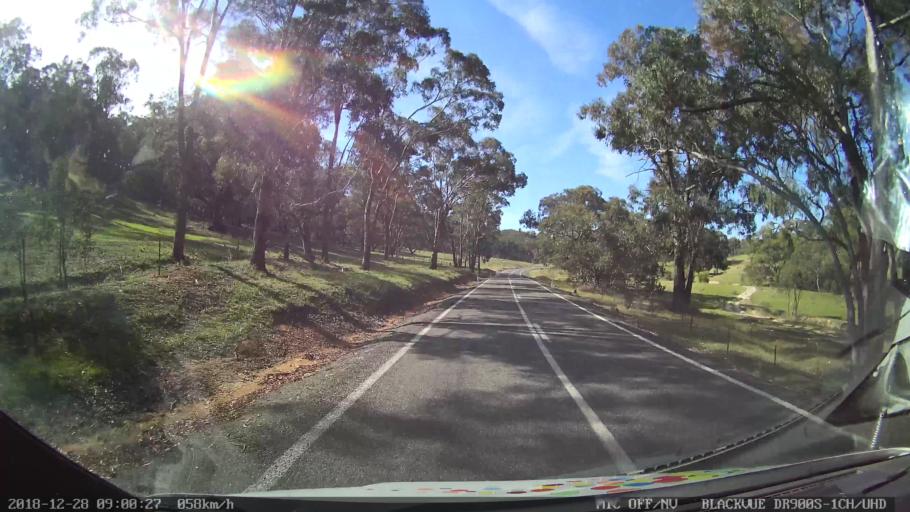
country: AU
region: New South Wales
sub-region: Upper Lachlan Shire
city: Crookwell
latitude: -34.1385
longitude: 149.3346
